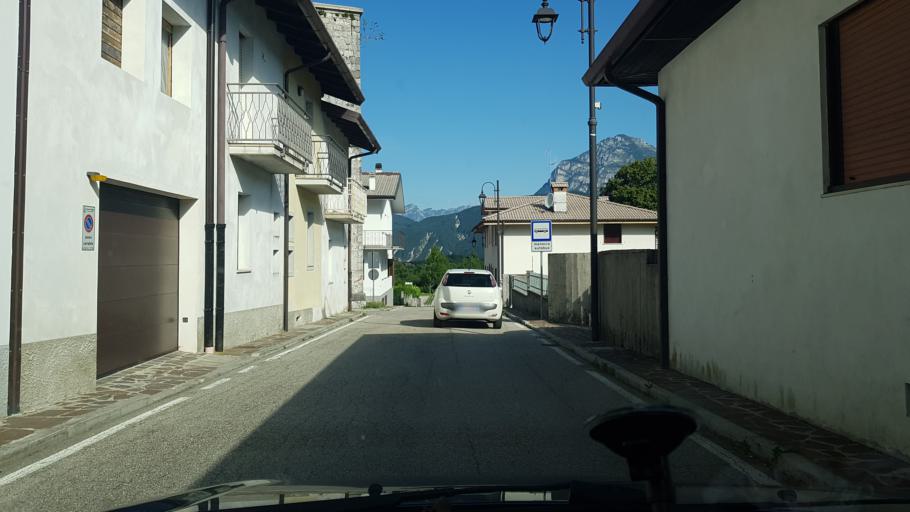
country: IT
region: Friuli Venezia Giulia
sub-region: Provincia di Udine
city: Prato
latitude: 46.3629
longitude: 13.3128
